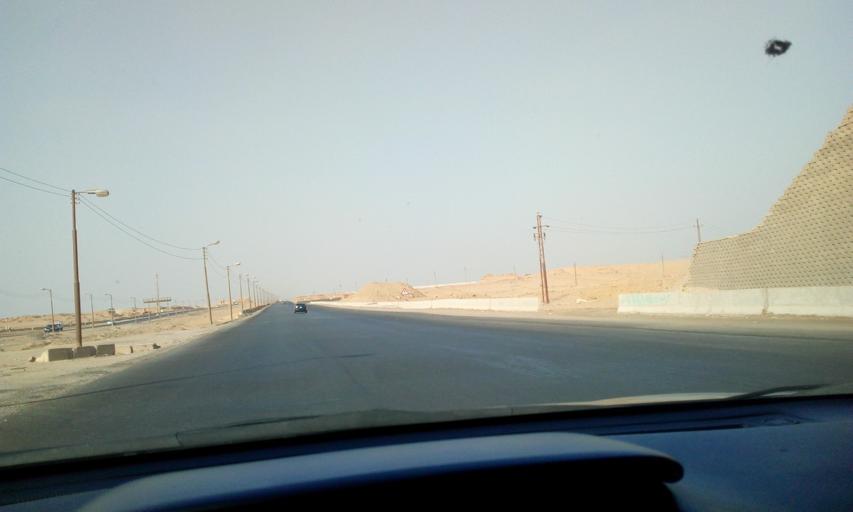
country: EG
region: Muhafazat al Fayyum
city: Tamiyah
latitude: 29.6265
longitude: 30.9603
